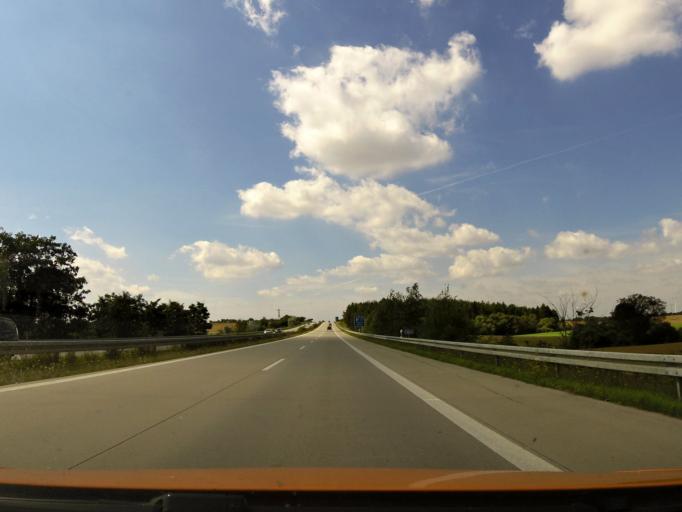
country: DE
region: Mecklenburg-Vorpommern
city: Penkun
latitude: 53.3187
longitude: 14.2936
